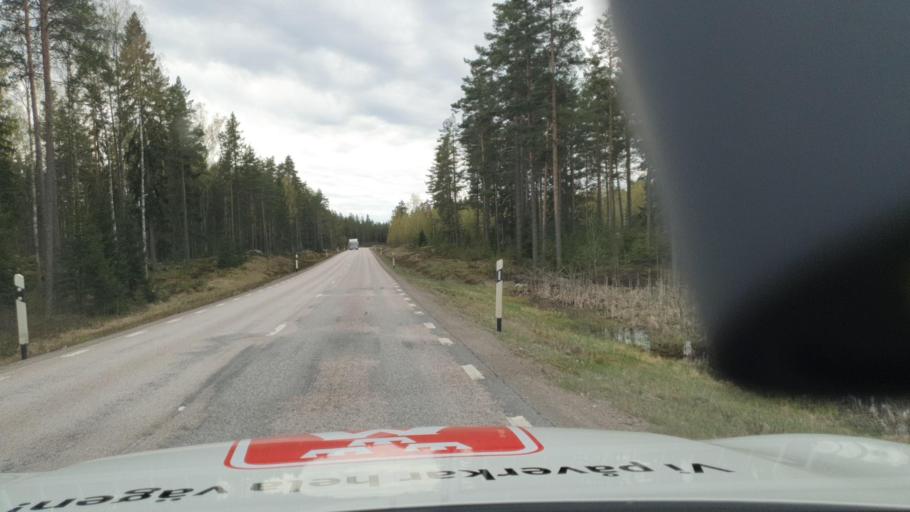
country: SE
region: Gaevleborg
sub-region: Gavle Kommun
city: Hedesunda
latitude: 60.4357
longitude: 17.1195
